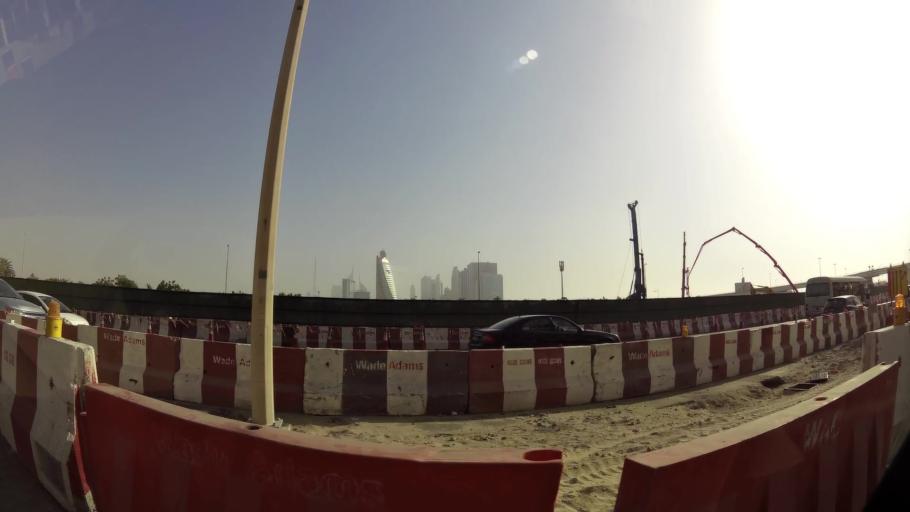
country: AE
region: Ash Shariqah
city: Sharjah
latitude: 25.2388
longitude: 55.2976
